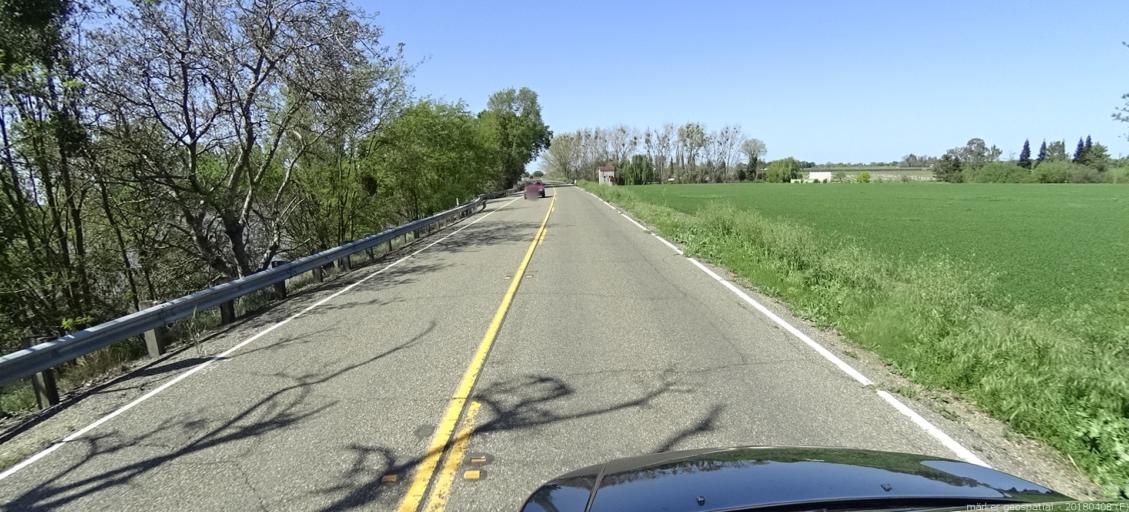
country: US
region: California
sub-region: Sacramento County
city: Laguna
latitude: 38.3707
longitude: -121.5209
